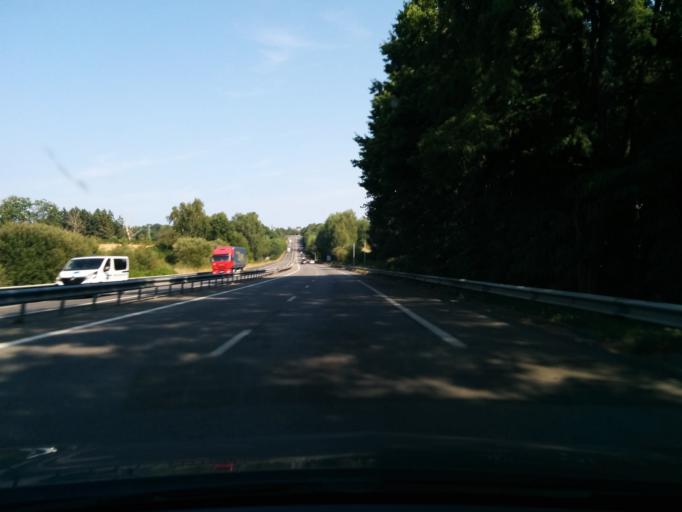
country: FR
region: Limousin
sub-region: Departement de la Haute-Vienne
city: Boisseuil
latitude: 45.7724
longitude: 1.3124
